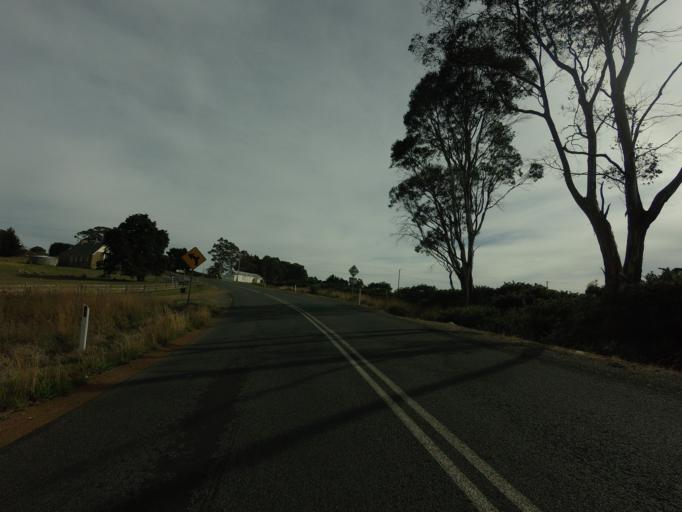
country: AU
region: Tasmania
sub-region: Sorell
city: Sorell
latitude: -42.4020
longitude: 147.4505
